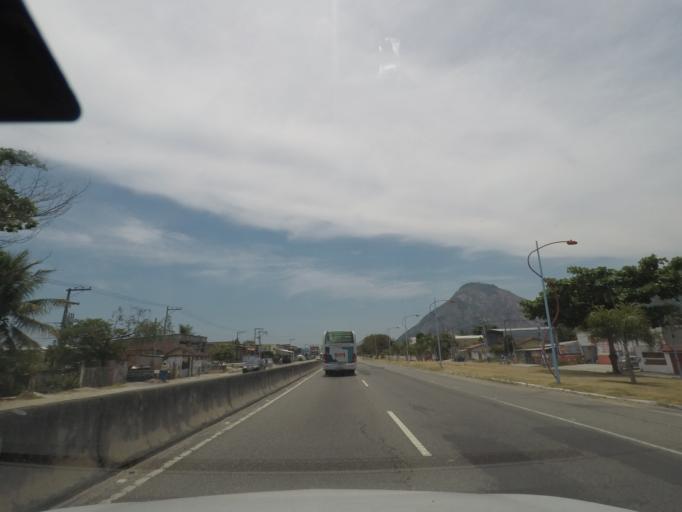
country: BR
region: Rio de Janeiro
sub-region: Marica
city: Marica
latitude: -22.9320
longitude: -42.8850
